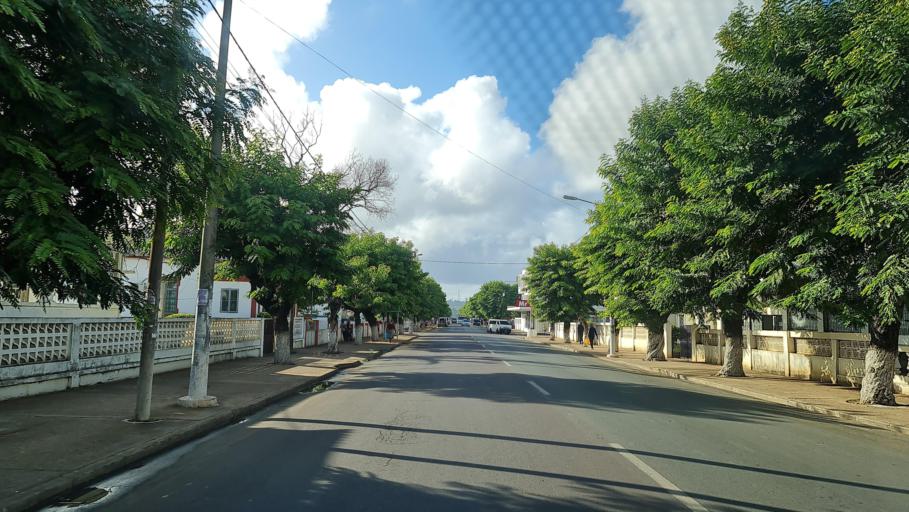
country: MZ
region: Gaza
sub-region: Xai-Xai District
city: Xai-Xai
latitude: -25.0391
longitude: 33.6393
